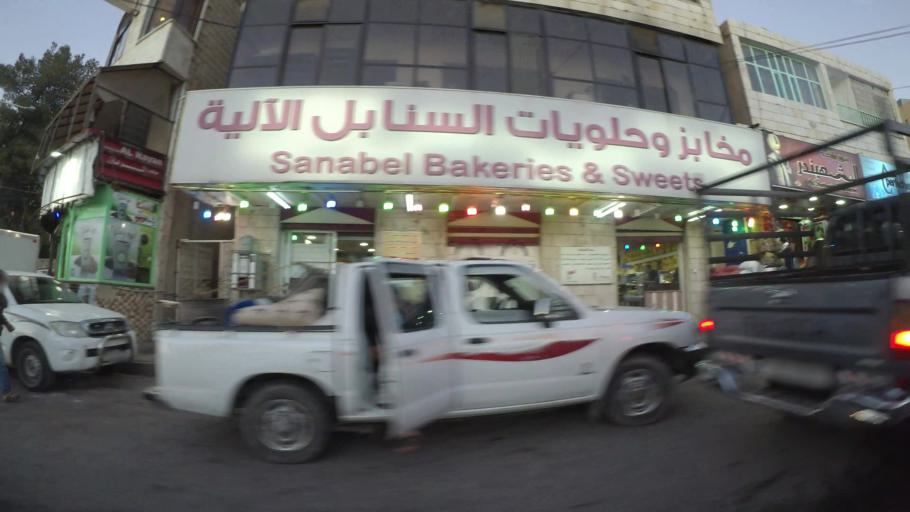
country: JO
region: Ma'an
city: Petra
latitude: 30.3218
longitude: 35.4786
